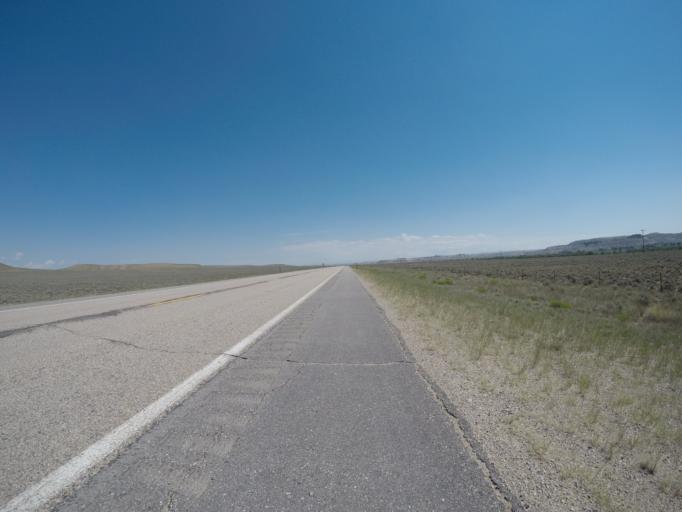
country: US
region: Wyoming
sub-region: Sublette County
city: Marbleton
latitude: 42.4286
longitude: -110.1083
